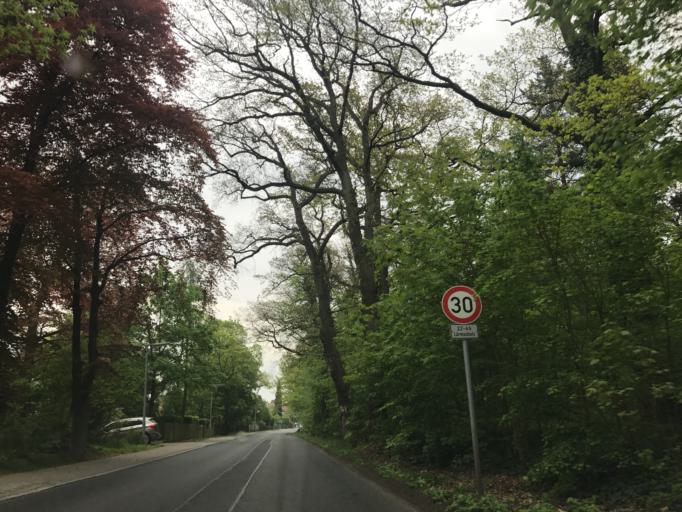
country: DE
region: Berlin
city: Spandau
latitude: 52.5576
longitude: 13.1844
